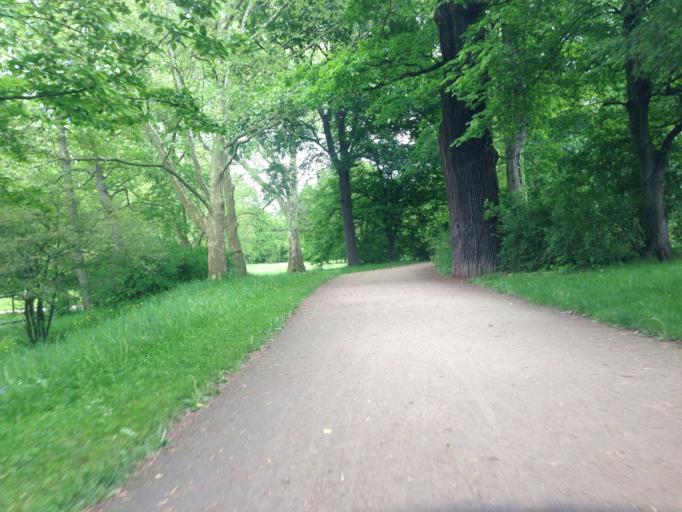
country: DE
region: Saxony
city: Dresden
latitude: 51.0384
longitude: 13.7552
